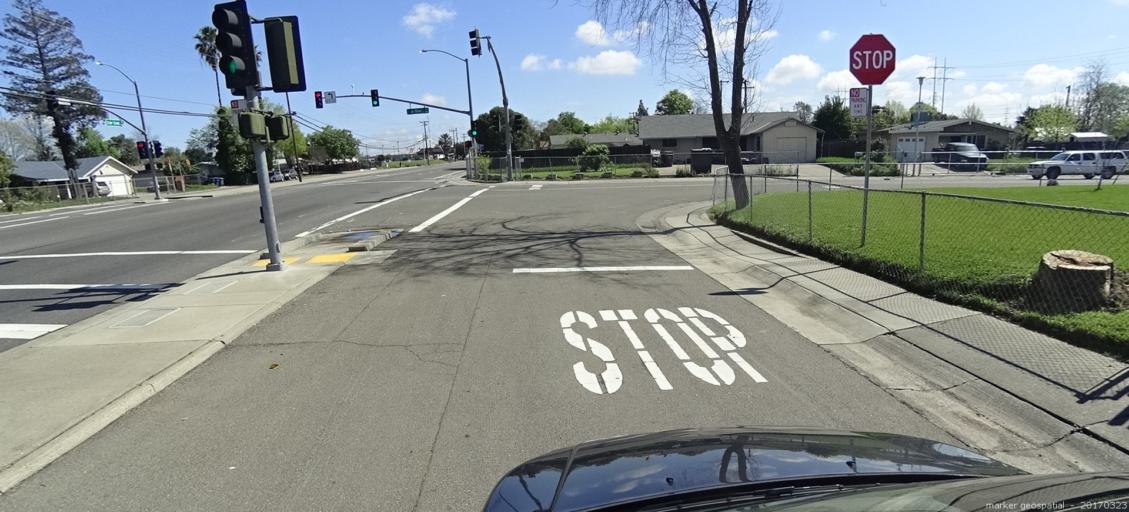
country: US
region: California
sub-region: Sacramento County
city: Florin
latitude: 38.5104
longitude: -121.4126
